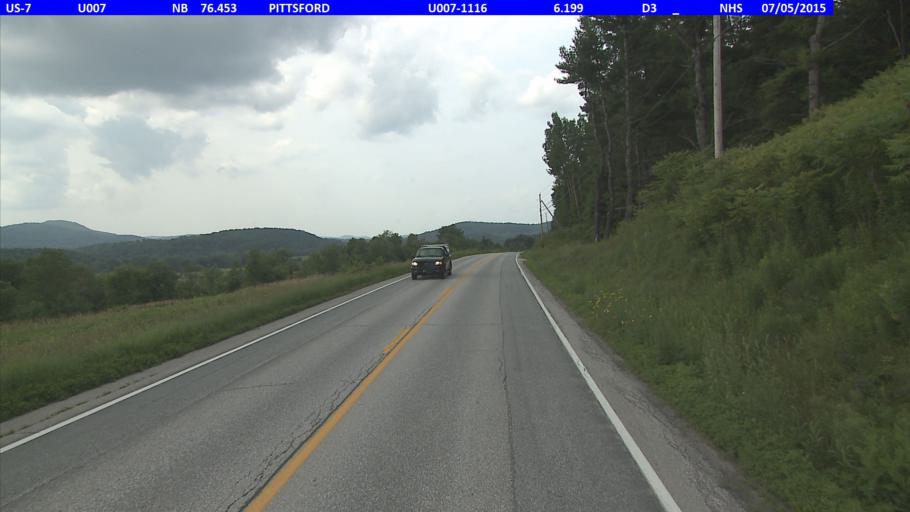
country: US
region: Vermont
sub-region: Rutland County
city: Brandon
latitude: 43.7364
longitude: -73.0417
